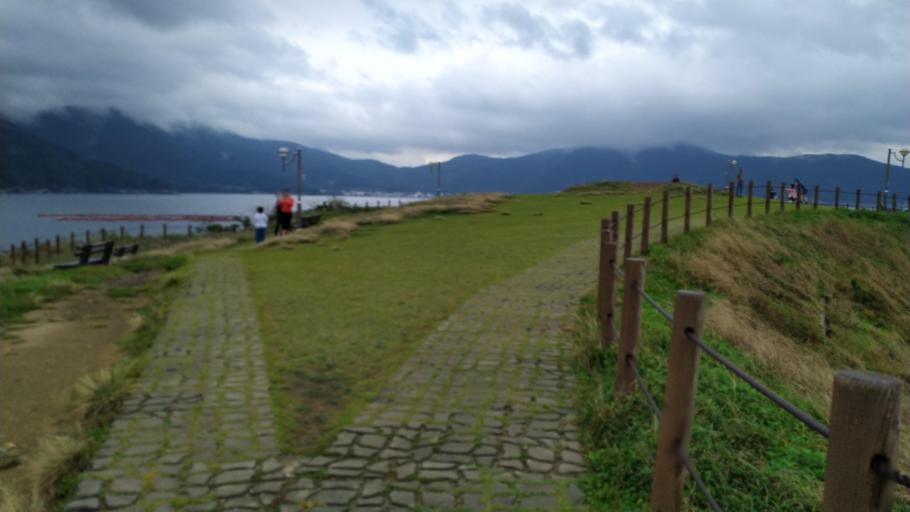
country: KR
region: Gyeongsangnam-do
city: Kyosai
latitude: 34.7442
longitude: 128.6633
